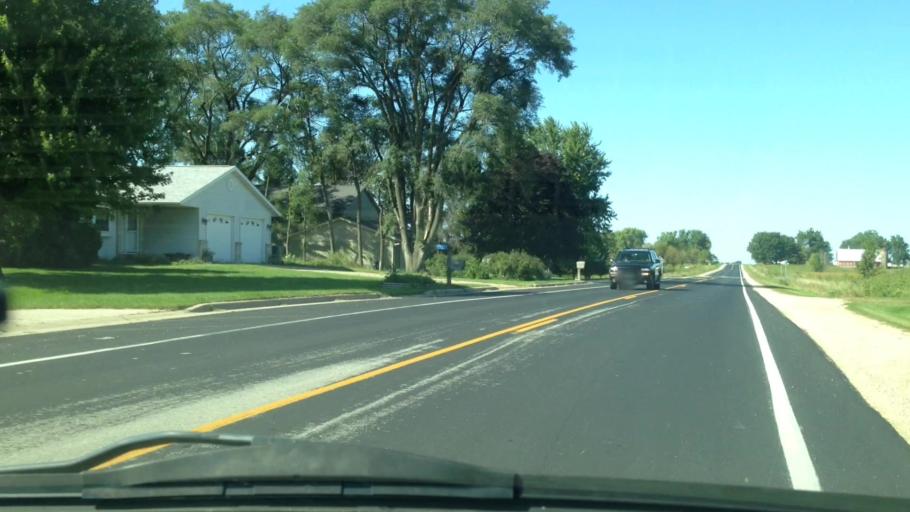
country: US
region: Minnesota
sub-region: Winona County
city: Lewiston
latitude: 43.9406
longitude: -91.7901
